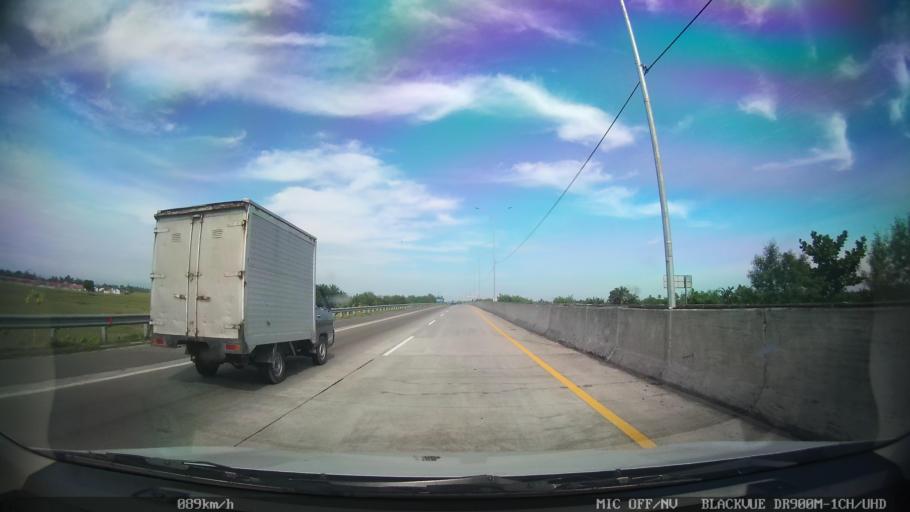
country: ID
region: North Sumatra
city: Sunggal
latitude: 3.6423
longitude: 98.5649
